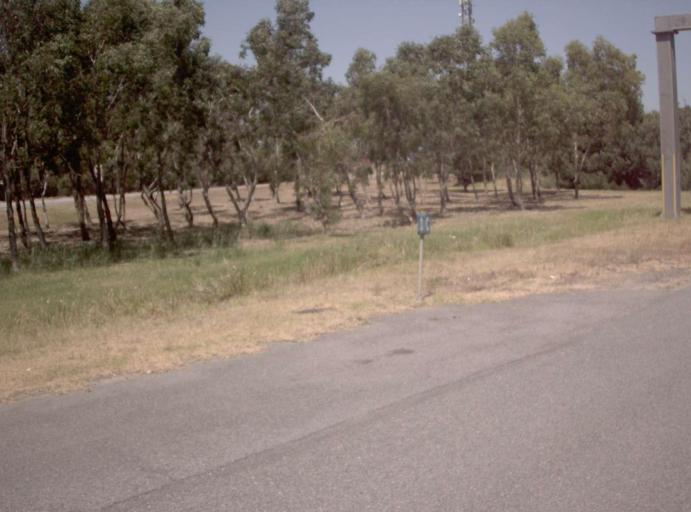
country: AU
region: Victoria
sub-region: Frankston
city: Seaford
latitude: -38.0960
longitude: 145.1478
